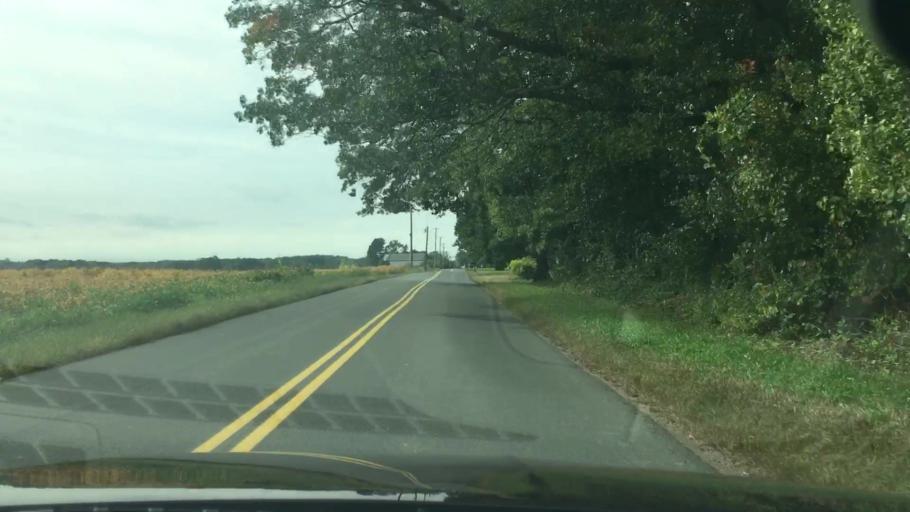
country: US
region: Connecticut
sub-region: Hartford County
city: Broad Brook
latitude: 41.8971
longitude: -72.5216
